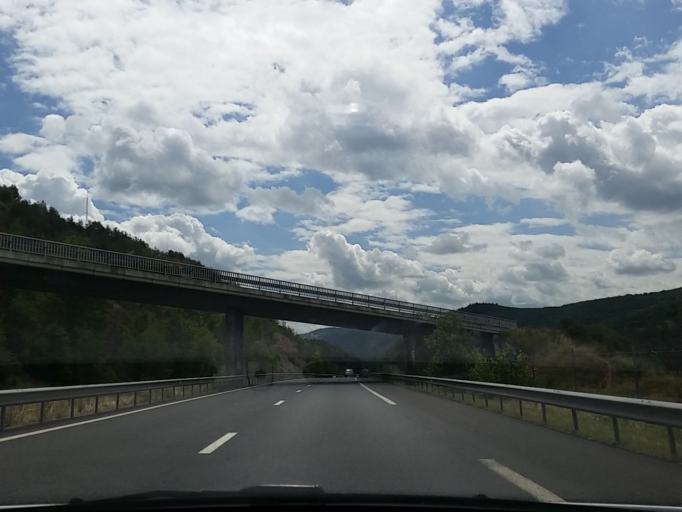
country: FR
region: Auvergne
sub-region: Departement du Cantal
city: Massiac
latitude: 45.2514
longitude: 3.2044
